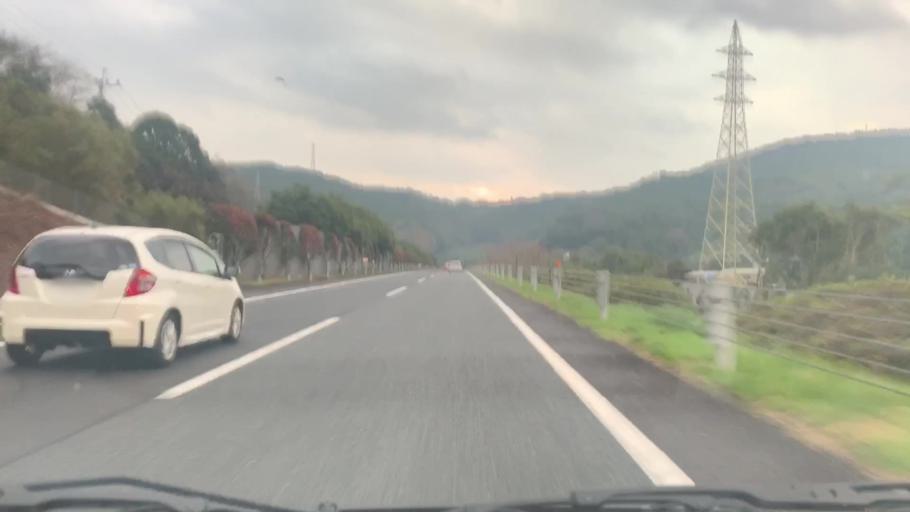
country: JP
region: Nagasaki
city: Omura
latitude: 32.8800
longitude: 129.9963
